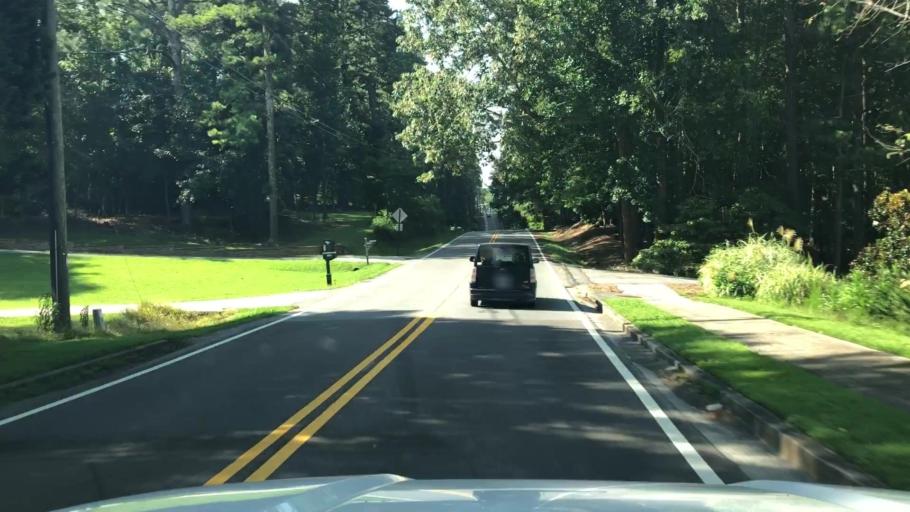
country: US
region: Georgia
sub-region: Cobb County
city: Fair Oaks
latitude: 33.9175
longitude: -84.5970
